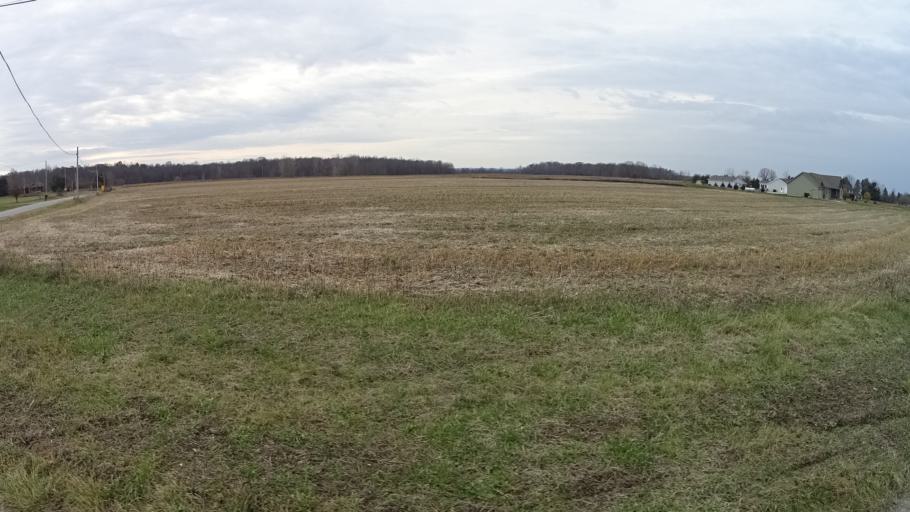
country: US
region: Ohio
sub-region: Lorain County
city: Lagrange
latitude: 41.1538
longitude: -82.0740
